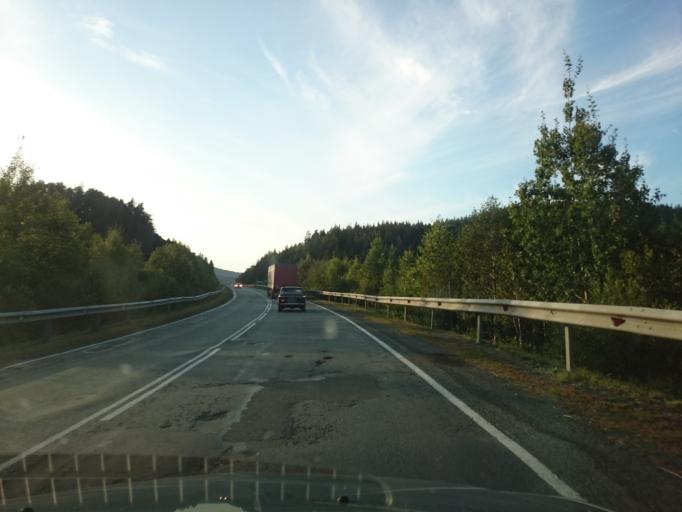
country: RU
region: Bashkortostan
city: Inzer
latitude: 53.9709
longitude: 57.8751
